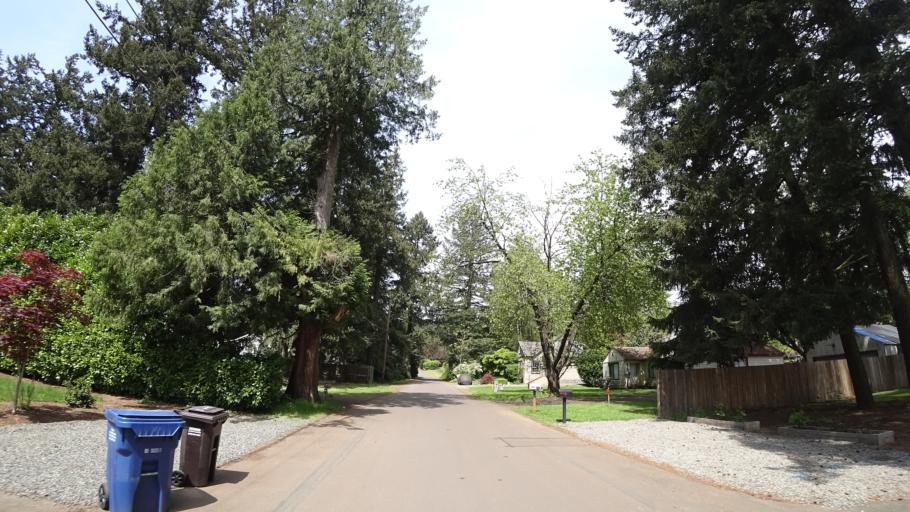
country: US
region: Oregon
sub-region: Clackamas County
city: Milwaukie
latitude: 45.4606
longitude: -122.6049
